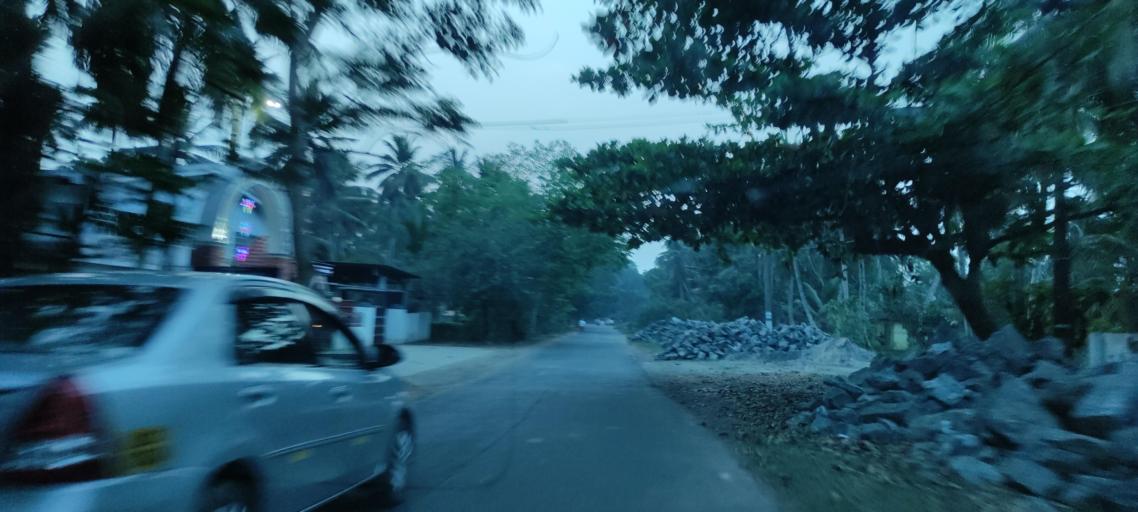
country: IN
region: Kerala
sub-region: Alappuzha
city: Mavelikara
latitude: 9.3300
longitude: 76.4816
